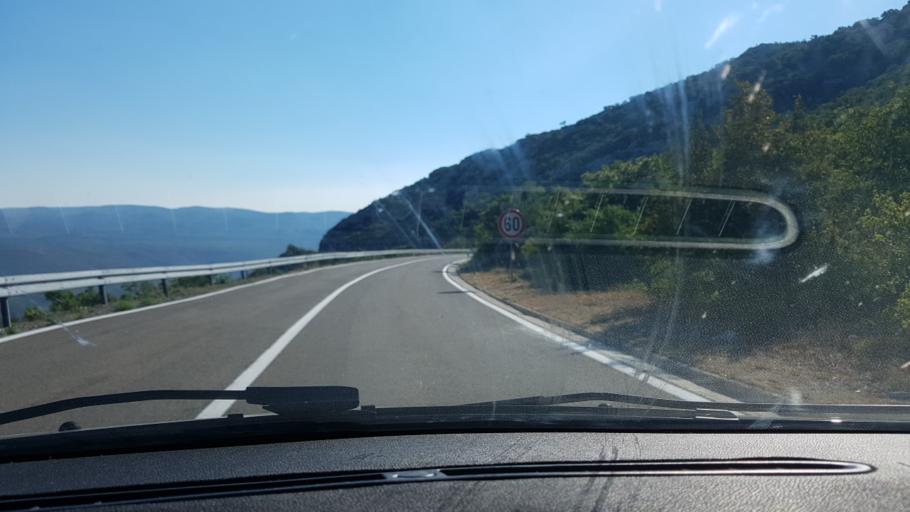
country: HR
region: Zadarska
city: Gracac
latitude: 44.2296
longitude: 15.7959
